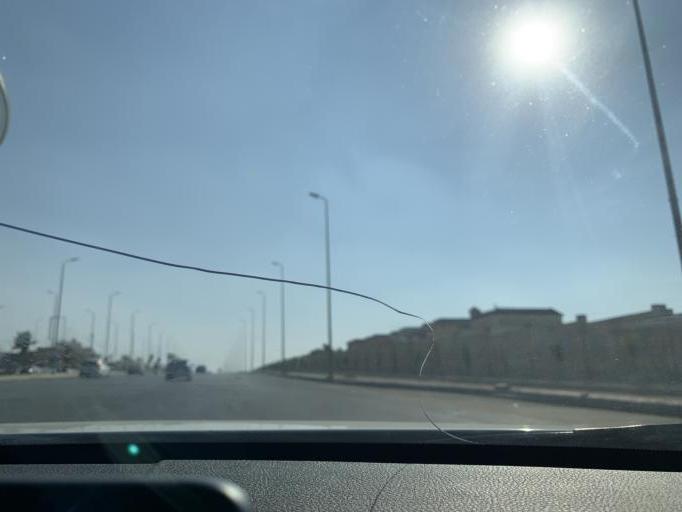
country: EG
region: Muhafazat al Qalyubiyah
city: Al Khankah
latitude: 30.0201
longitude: 31.4746
